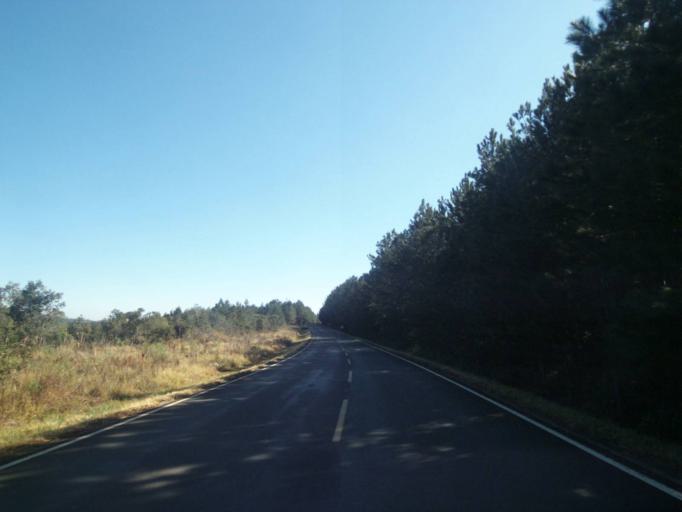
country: BR
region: Parana
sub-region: Tibagi
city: Tibagi
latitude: -24.4510
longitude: -50.5460
